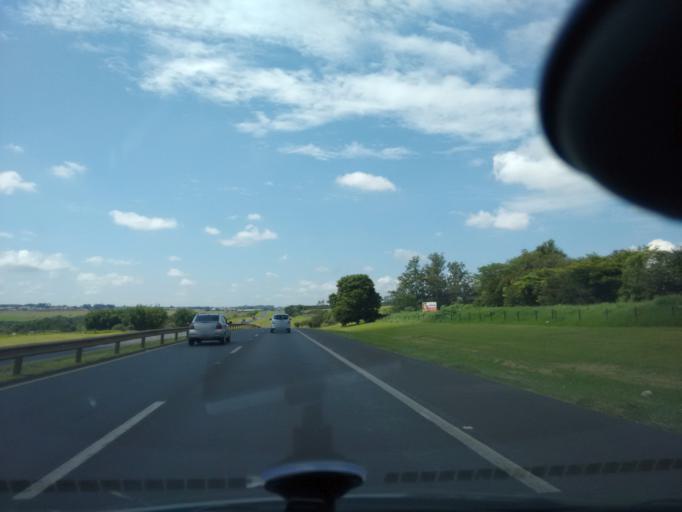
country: BR
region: Sao Paulo
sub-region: Sao Carlos
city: Sao Carlos
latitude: -21.9791
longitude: -47.9243
